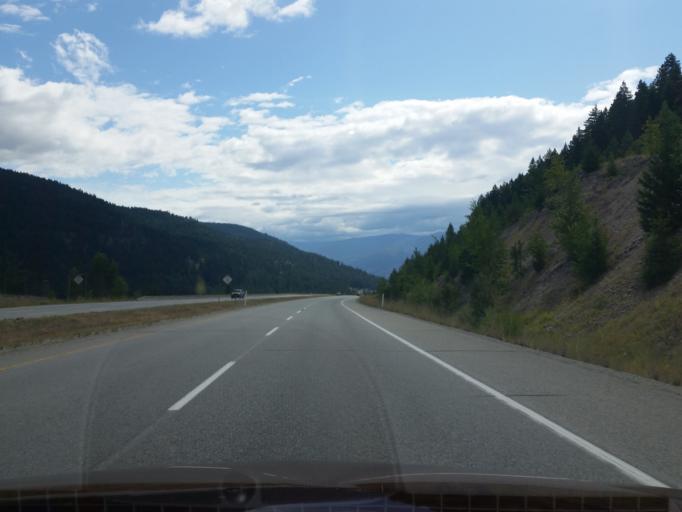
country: CA
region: British Columbia
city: Peachland
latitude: 49.8162
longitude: -119.7710
